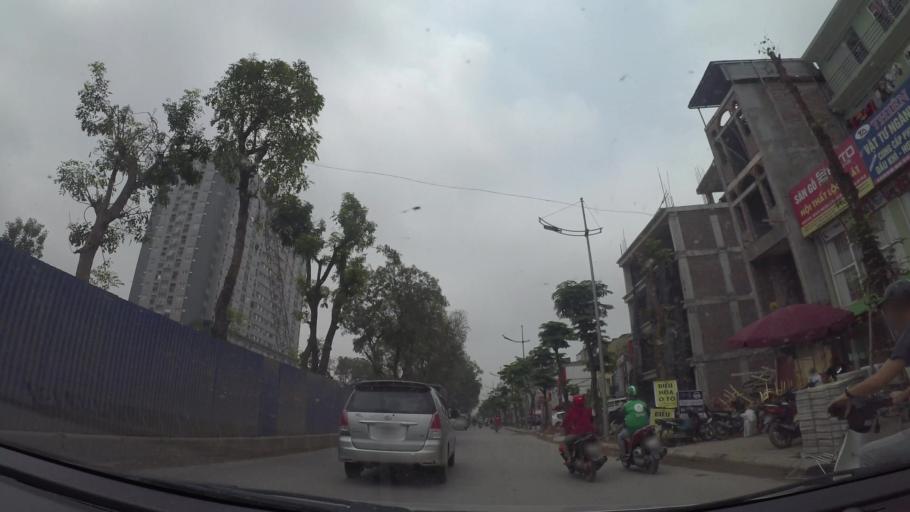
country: VN
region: Ha Noi
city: Cau Dien
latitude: 21.0446
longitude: 105.7809
